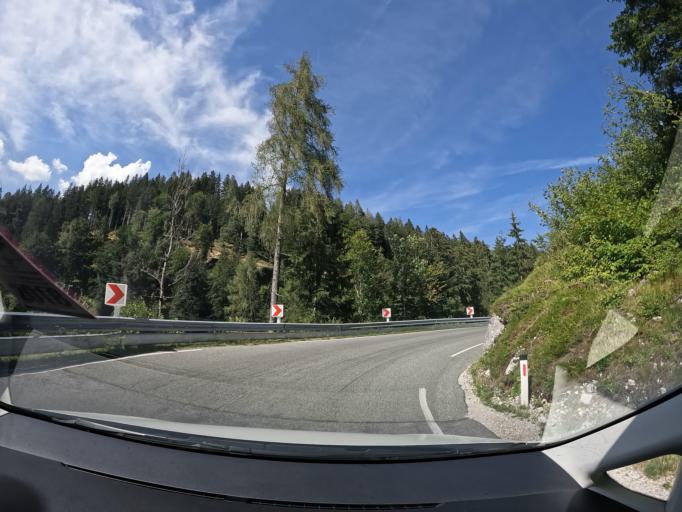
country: AT
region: Carinthia
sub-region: Politischer Bezirk Klagenfurt Land
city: Schiefling am See
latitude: 46.6142
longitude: 14.1032
